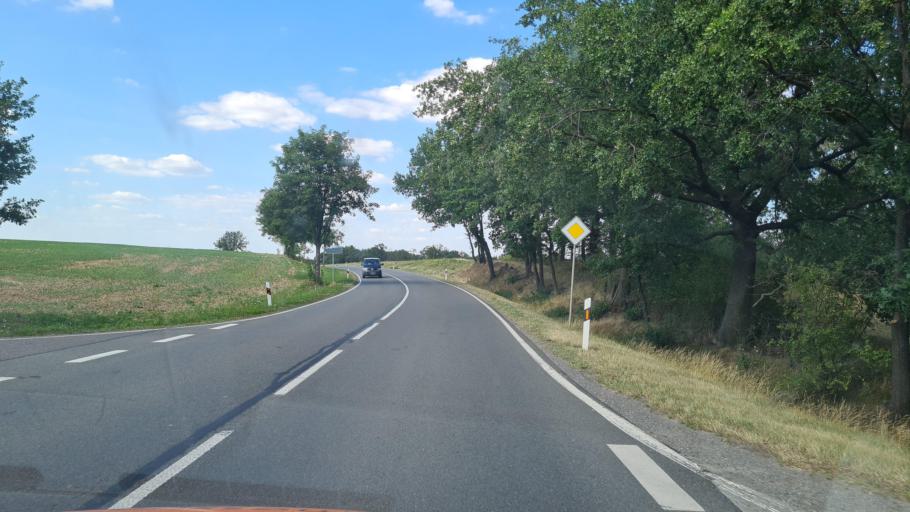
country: DE
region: Saxony
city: Machern
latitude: 51.4031
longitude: 12.6451
